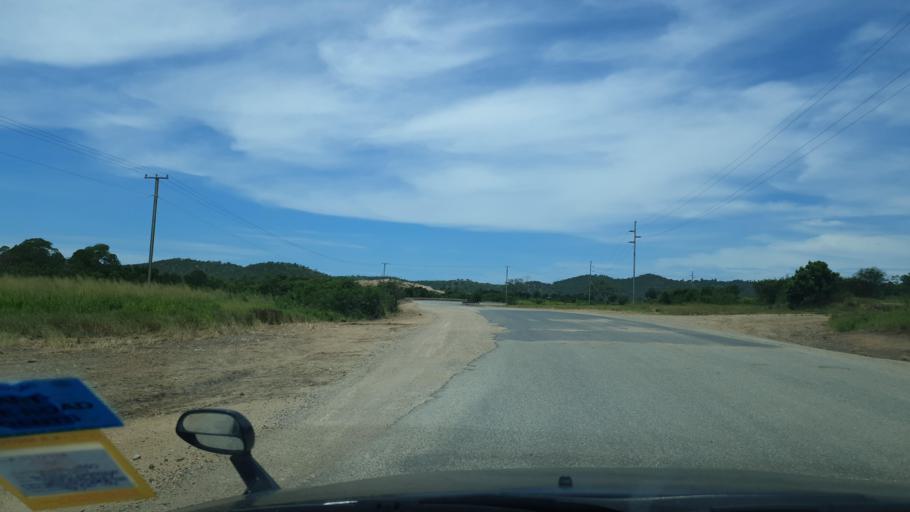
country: PG
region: National Capital
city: Port Moresby
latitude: -9.4192
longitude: 147.0944
